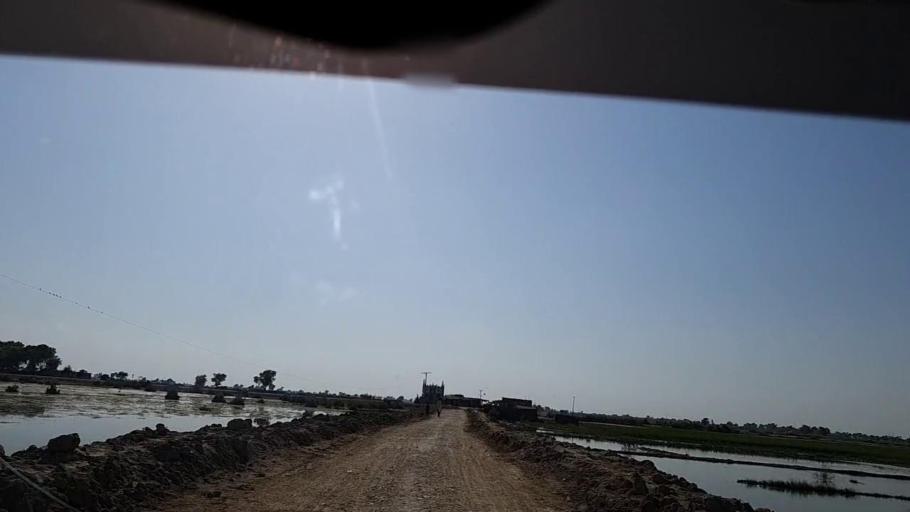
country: PK
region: Sindh
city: Tangwani
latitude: 28.3622
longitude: 69.0154
